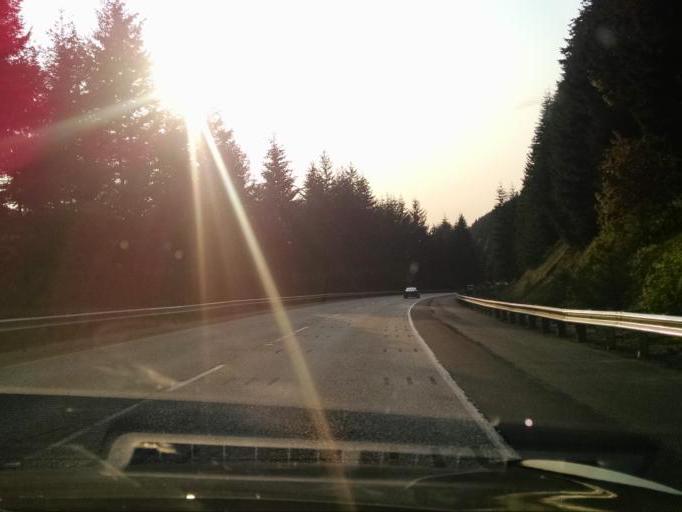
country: US
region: Washington
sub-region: Whatcom County
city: Geneva
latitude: 48.6891
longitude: -122.4248
